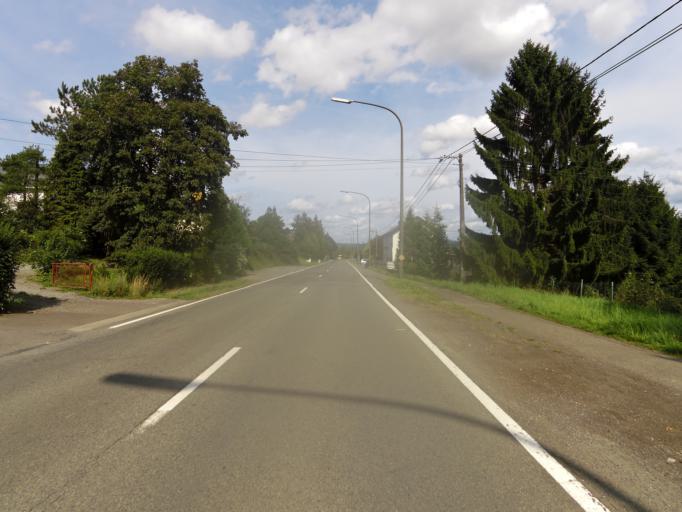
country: BE
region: Wallonia
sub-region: Province du Luxembourg
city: Durbuy
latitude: 50.3459
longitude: 5.4757
